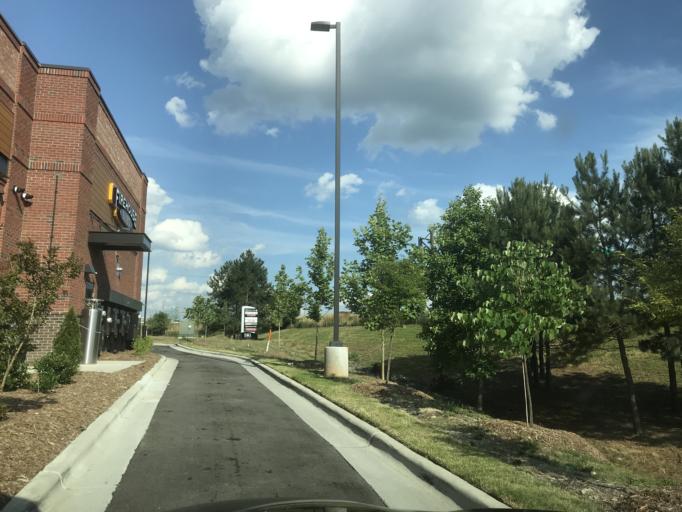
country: US
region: North Carolina
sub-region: Wake County
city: Wake Forest
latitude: 35.9695
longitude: -78.5473
